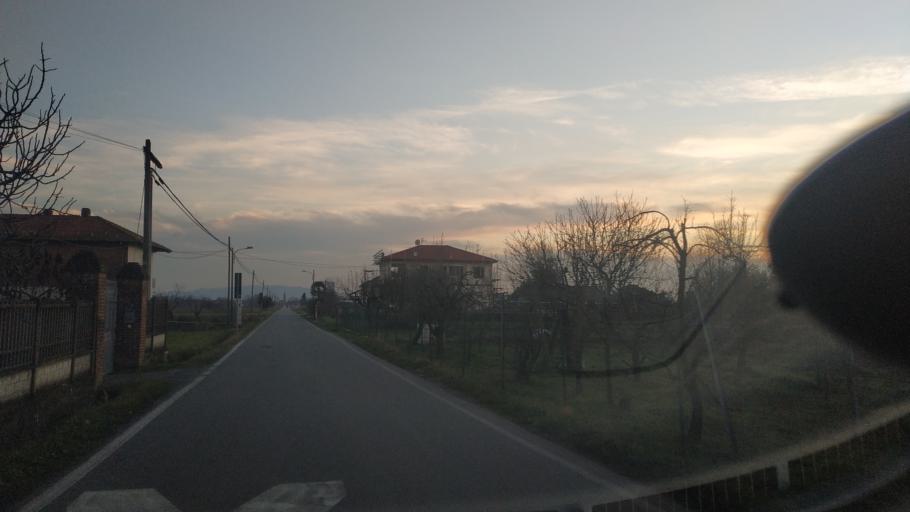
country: IT
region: Piedmont
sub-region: Provincia di Torino
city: Caluso
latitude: 45.2783
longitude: 7.8778
